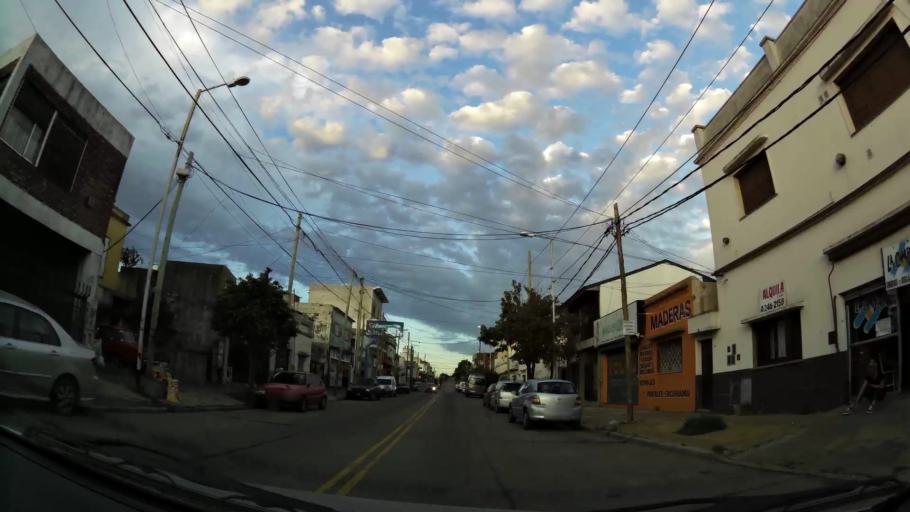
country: AR
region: Buenos Aires
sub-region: Partido de Avellaneda
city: Avellaneda
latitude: -34.6996
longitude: -58.3293
